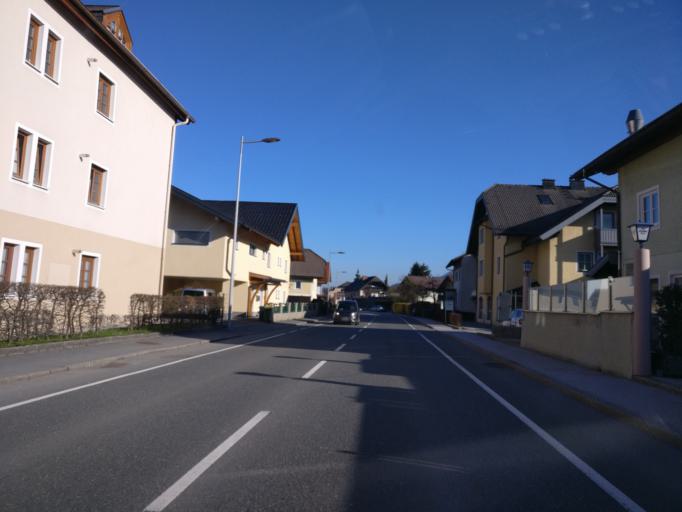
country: AT
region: Salzburg
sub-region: Politischer Bezirk Hallein
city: Oberalm
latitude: 47.6954
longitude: 13.1007
